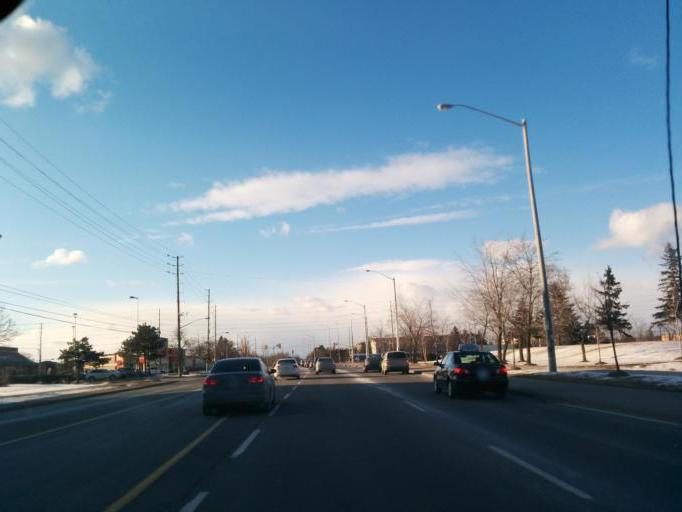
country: CA
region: Ontario
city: Brampton
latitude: 43.6552
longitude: -79.7419
